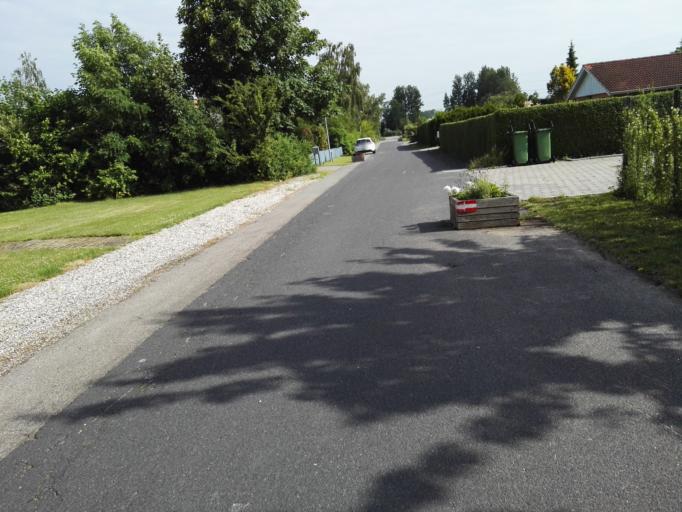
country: DK
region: Zealand
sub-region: Roskilde Kommune
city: Jyllinge
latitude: 55.7713
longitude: 12.1067
